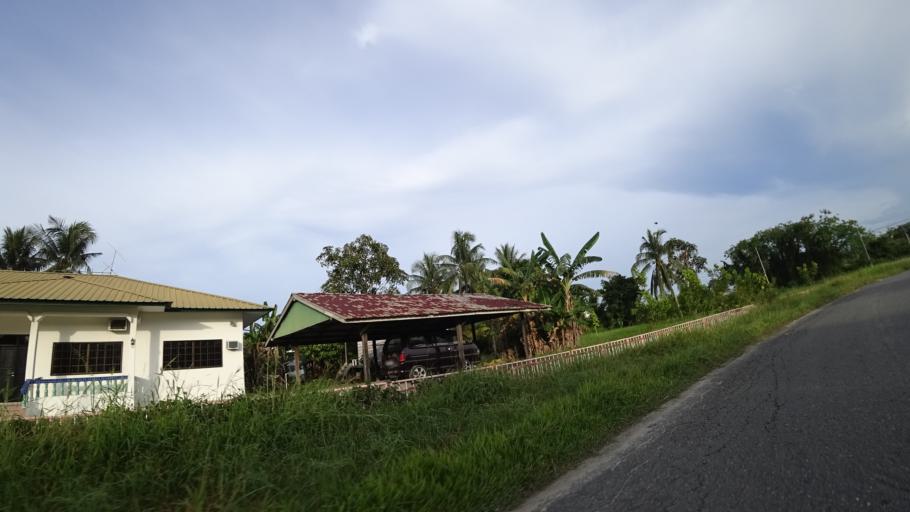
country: BN
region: Brunei and Muara
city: Bandar Seri Begawan
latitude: 4.8813
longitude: 114.8352
